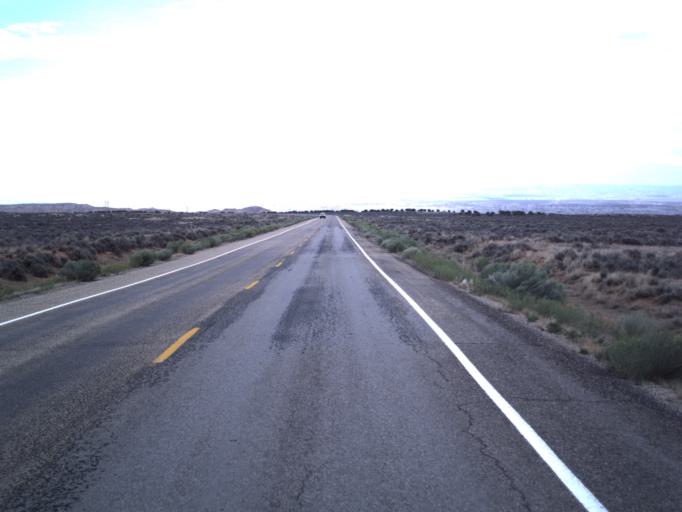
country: US
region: Utah
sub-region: Uintah County
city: Naples
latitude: 40.1460
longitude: -109.2900
